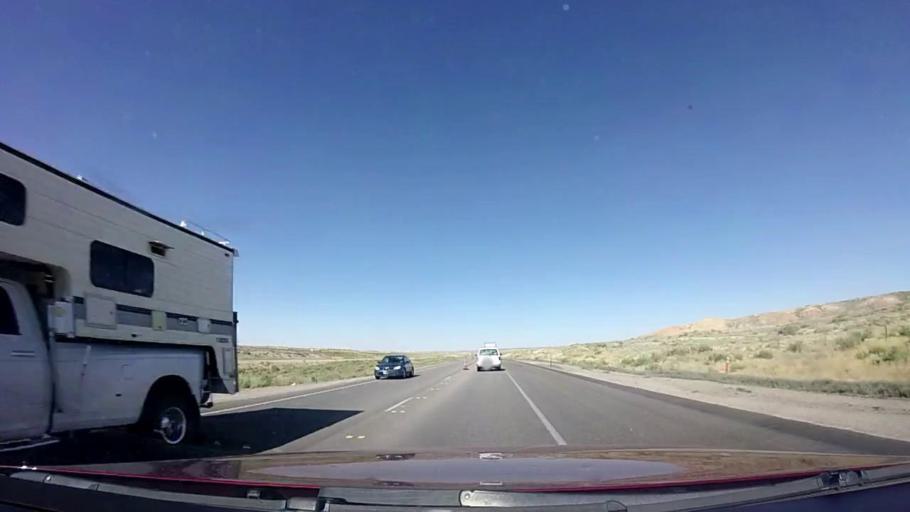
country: US
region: Wyoming
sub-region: Carbon County
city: Rawlins
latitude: 41.7065
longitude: -107.8677
